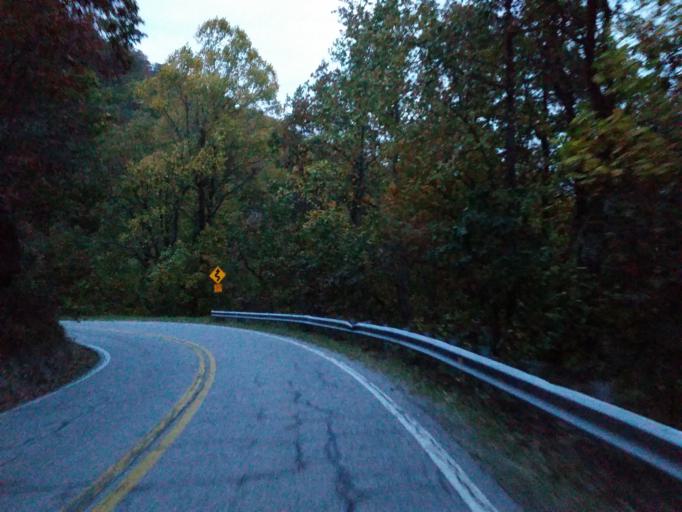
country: US
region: Georgia
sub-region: Lumpkin County
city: Dahlonega
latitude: 34.6466
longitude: -83.9648
